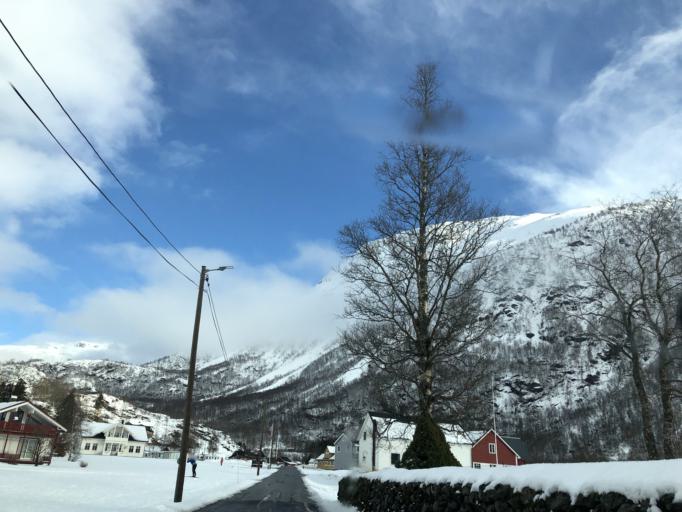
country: NO
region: Hordaland
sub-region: Odda
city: Odda
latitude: 59.8311
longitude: 6.8226
